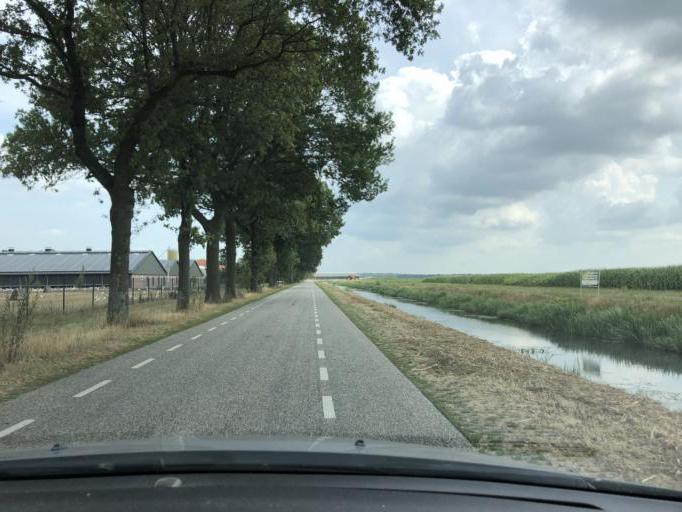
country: NL
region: Drenthe
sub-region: Gemeente Coevorden
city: Dalen
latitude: 52.7907
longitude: 6.6369
